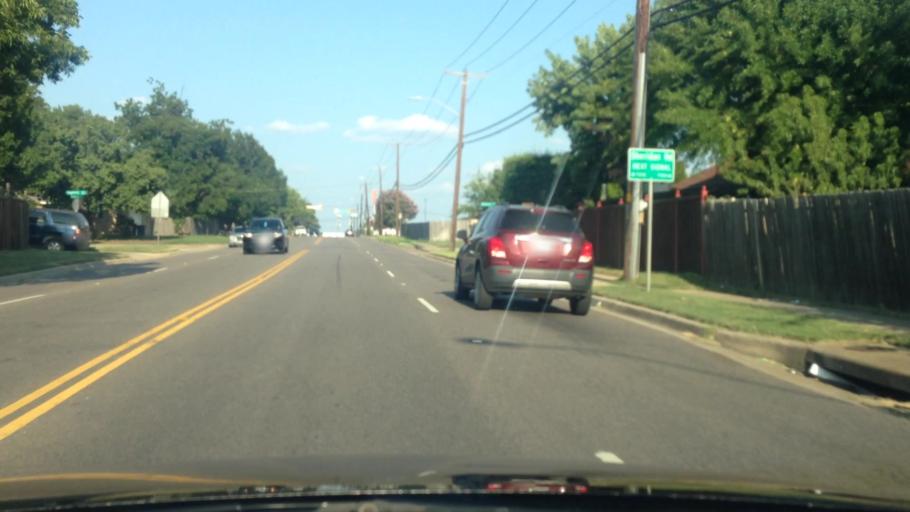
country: US
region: Texas
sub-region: Tarrant County
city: Edgecliff Village
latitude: 32.6351
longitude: -97.3271
